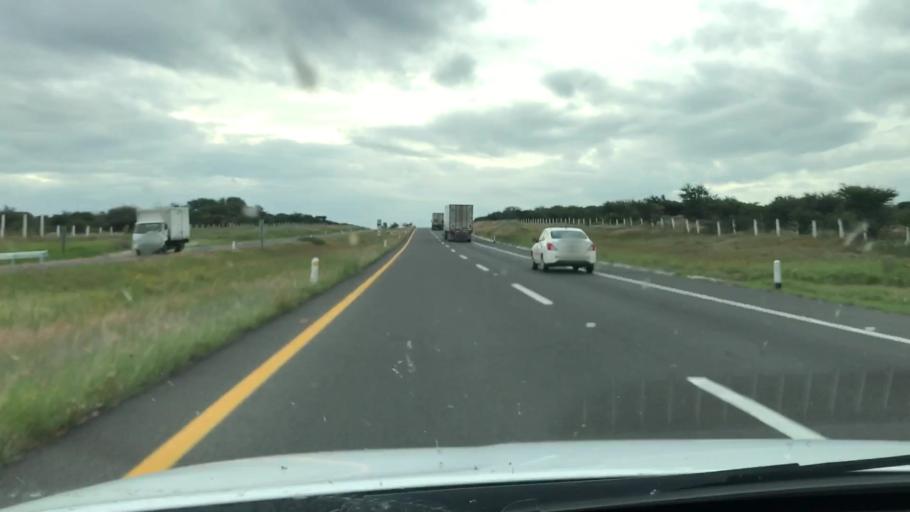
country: MX
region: Jalisco
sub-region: Lagos de Moreno
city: Cristeros [Fraccionamiento]
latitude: 21.2354
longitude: -101.9336
